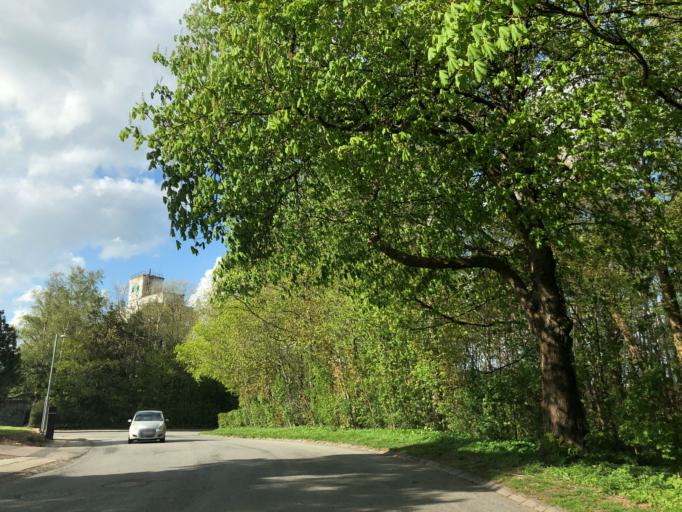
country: DK
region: Zealand
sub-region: Ringsted Kommune
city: Ringsted
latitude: 55.4329
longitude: 11.8014
